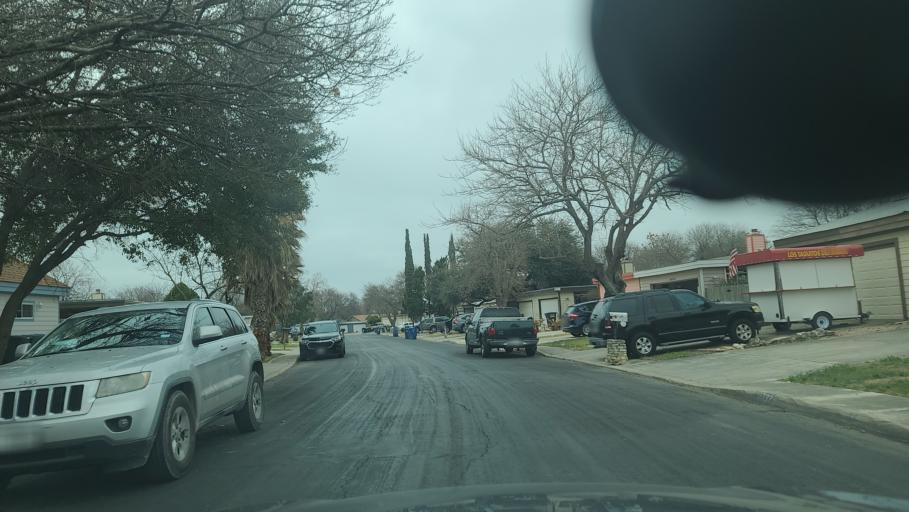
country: US
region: Texas
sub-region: Bexar County
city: Leon Valley
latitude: 29.5550
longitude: -98.6245
